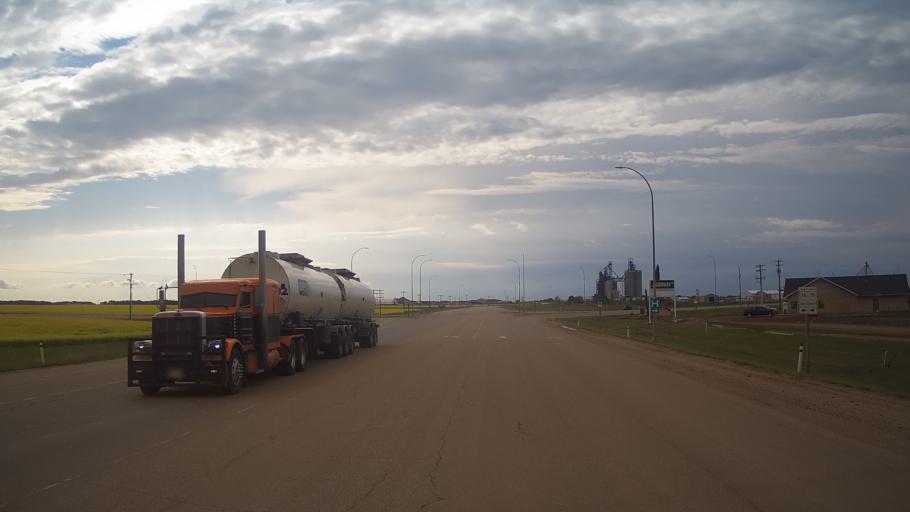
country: CA
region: Alberta
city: Viking
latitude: 53.0925
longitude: -111.7821
